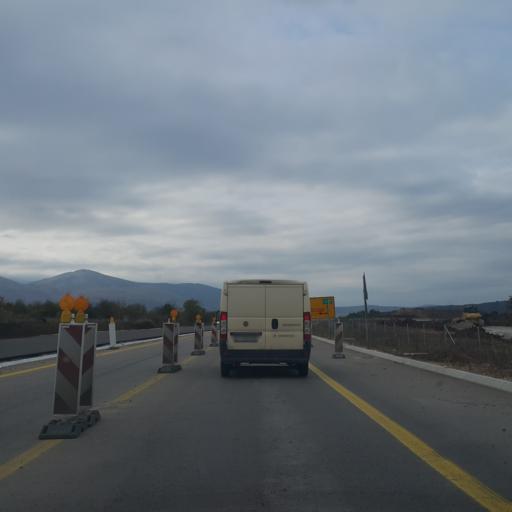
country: RS
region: Central Serbia
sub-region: Pirotski Okrug
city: Bela Palanka
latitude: 43.2248
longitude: 22.3925
